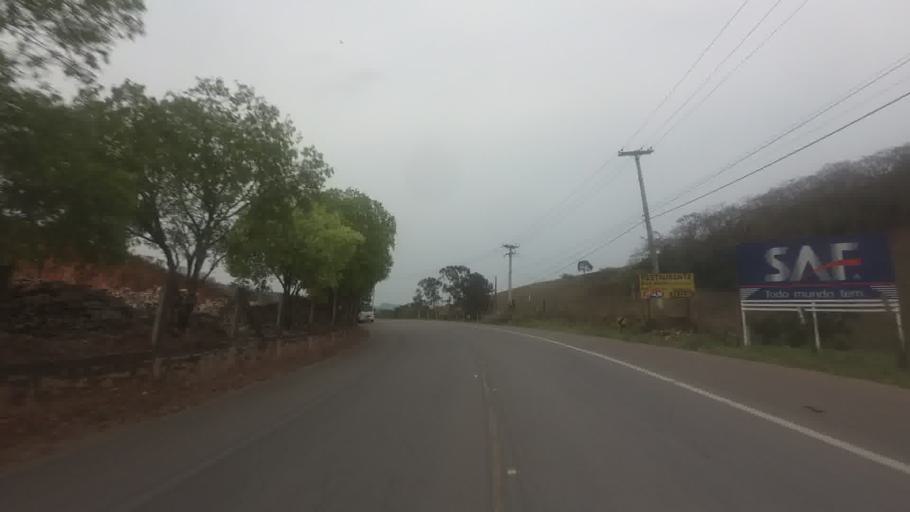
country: BR
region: Rio de Janeiro
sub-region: Santo Antonio De Padua
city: Santo Antonio de Padua
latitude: -21.6323
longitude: -42.2691
